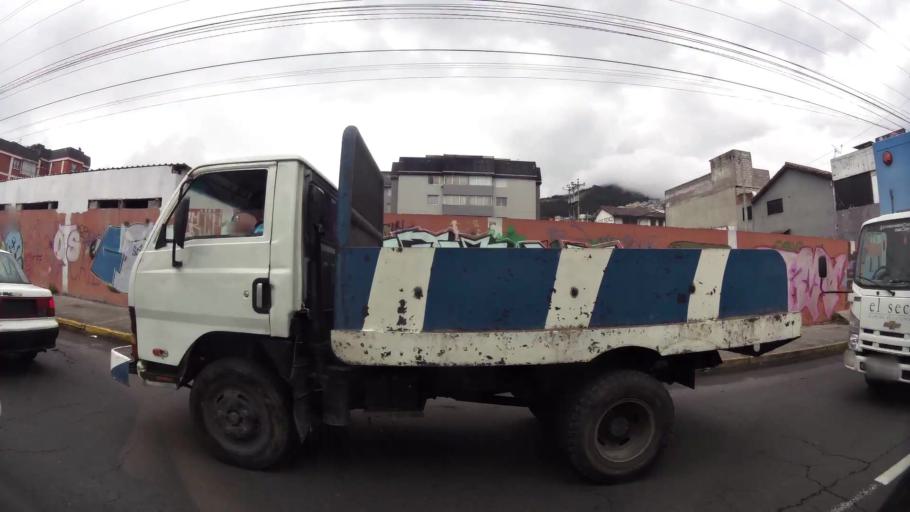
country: EC
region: Pichincha
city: Quito
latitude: -0.2697
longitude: -78.5518
